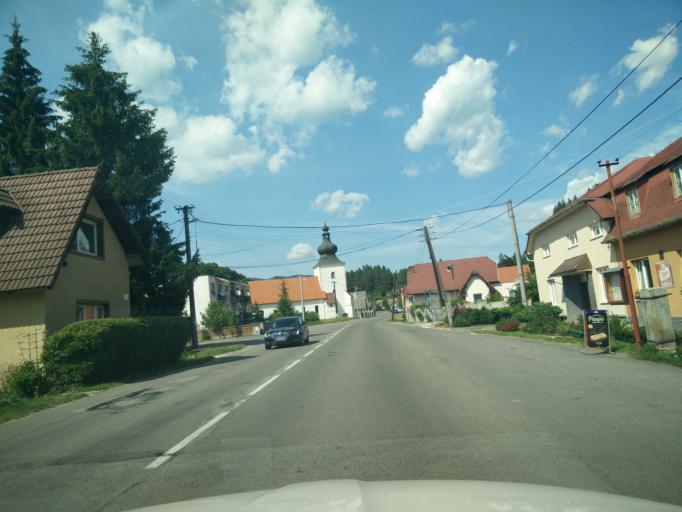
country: SK
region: Nitriansky
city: Prievidza
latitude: 48.8945
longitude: 18.6420
